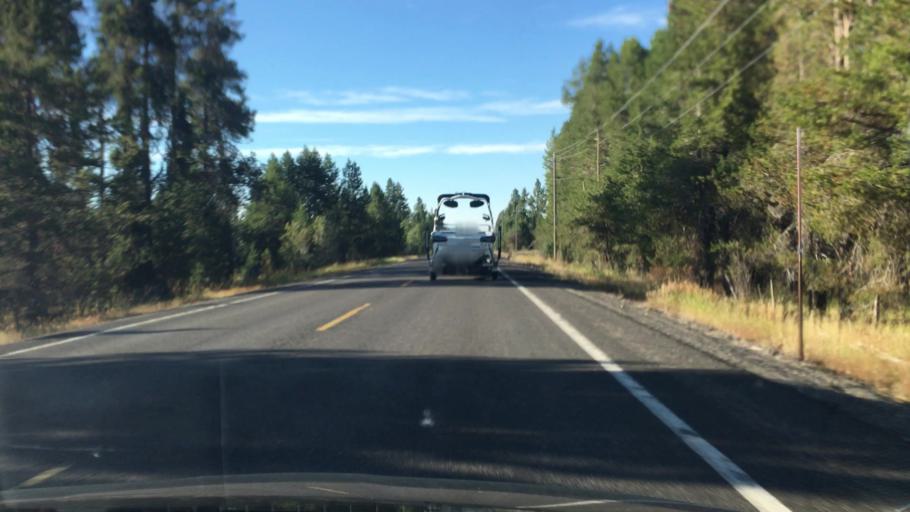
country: US
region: Idaho
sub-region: Valley County
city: Cascade
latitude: 44.4541
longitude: -115.9993
